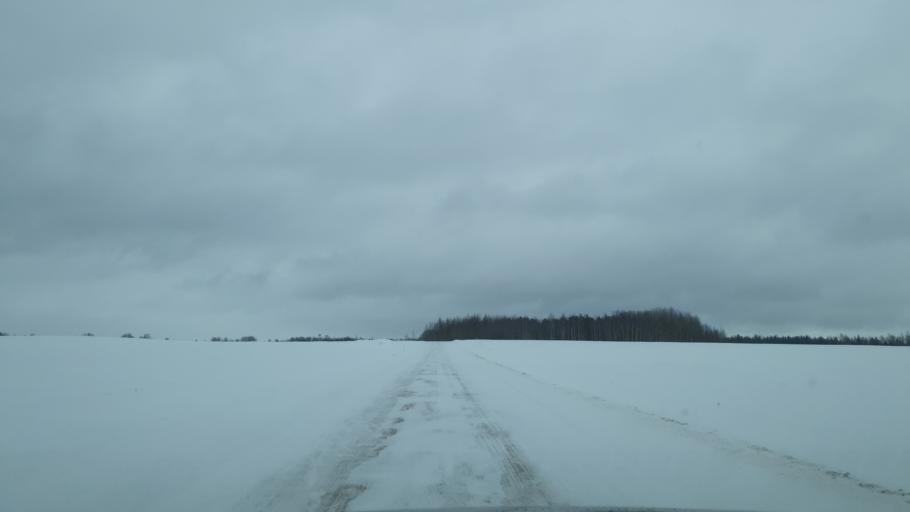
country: EE
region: Polvamaa
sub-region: Raepina vald
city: Rapina
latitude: 58.2029
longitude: 27.2735
